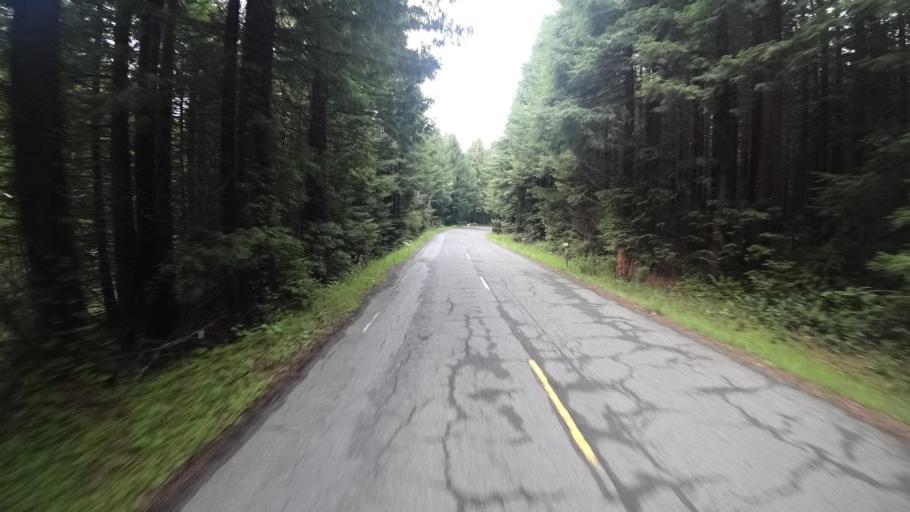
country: US
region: California
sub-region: Humboldt County
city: Blue Lake
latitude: 40.8734
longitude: -123.9690
